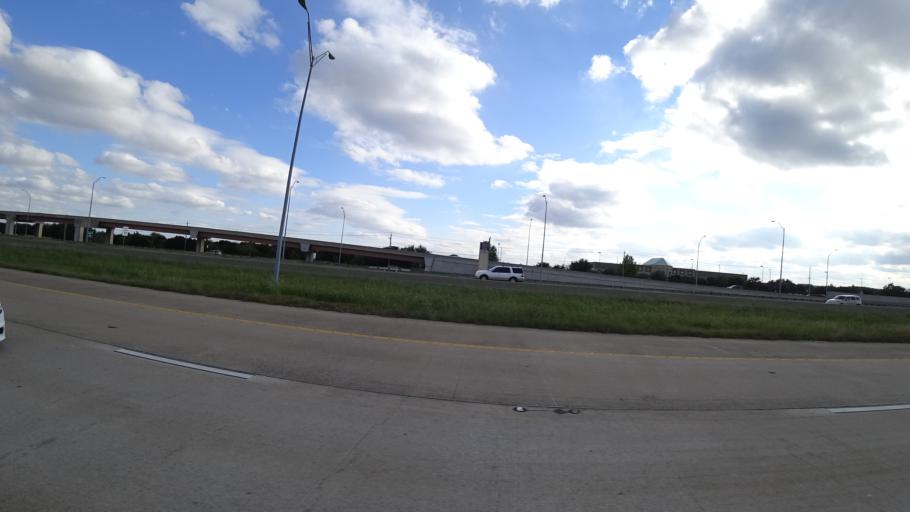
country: US
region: Texas
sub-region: Williamson County
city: Jollyville
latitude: 30.4749
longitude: -97.7728
